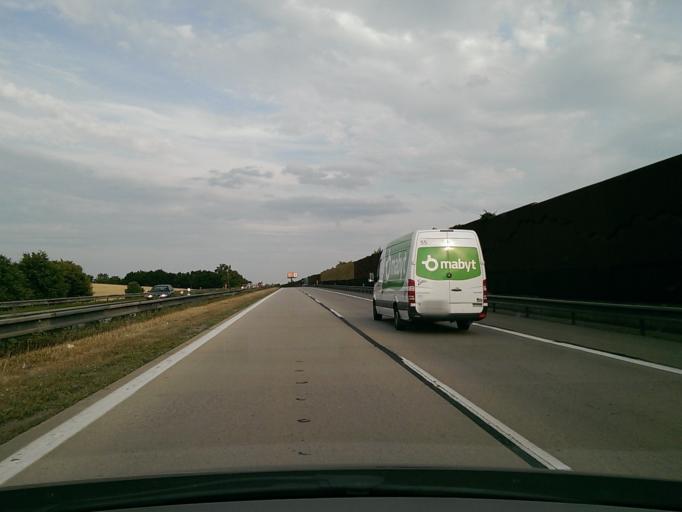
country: CZ
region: Vysocina
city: Merin
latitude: 49.3944
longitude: 15.8926
